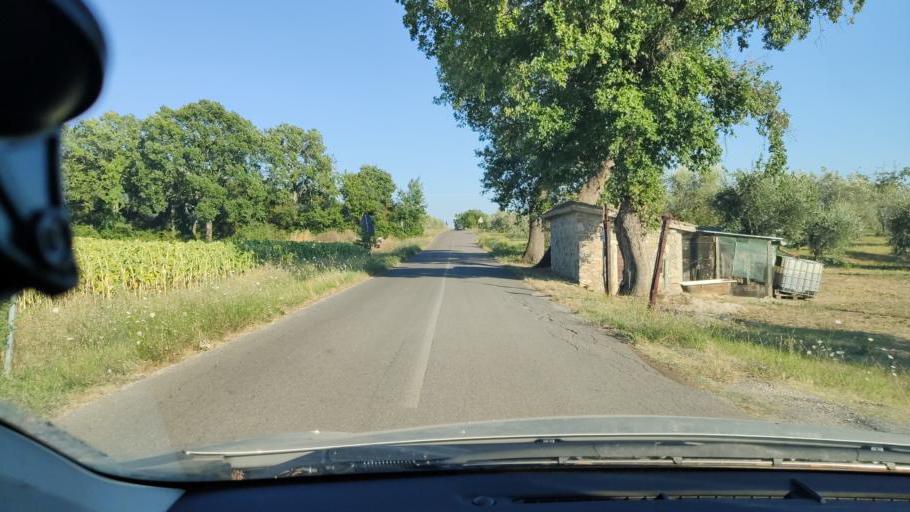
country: IT
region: Umbria
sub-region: Provincia di Terni
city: Lugnano in Teverina
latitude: 42.5471
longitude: 12.3502
